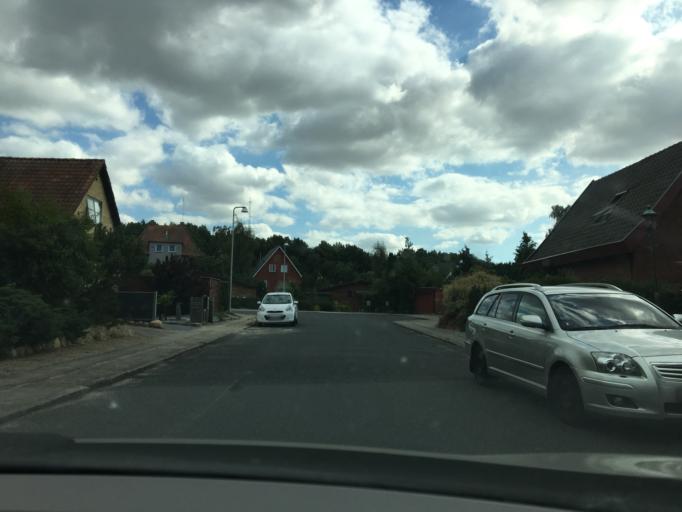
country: DK
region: South Denmark
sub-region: Odense Kommune
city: Odense
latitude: 55.3943
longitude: 10.3288
